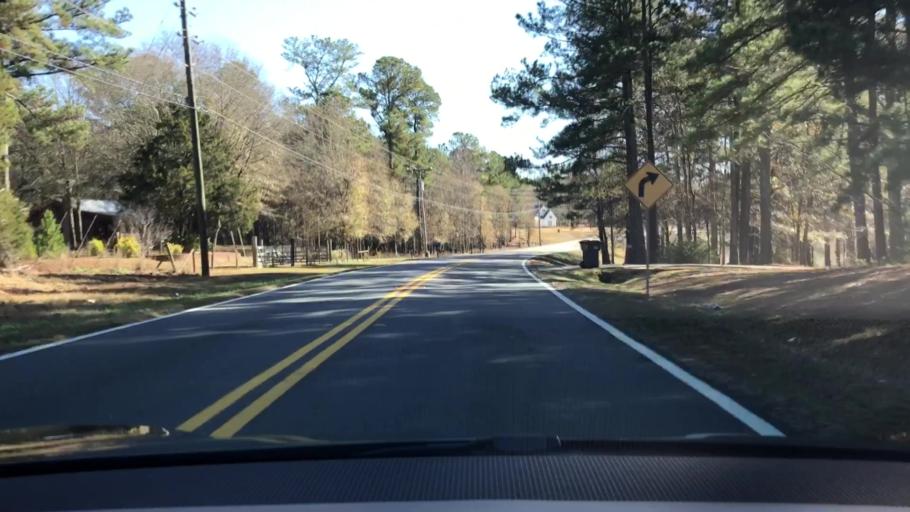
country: US
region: Georgia
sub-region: Walton County
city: Monroe
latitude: 33.8587
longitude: -83.7393
